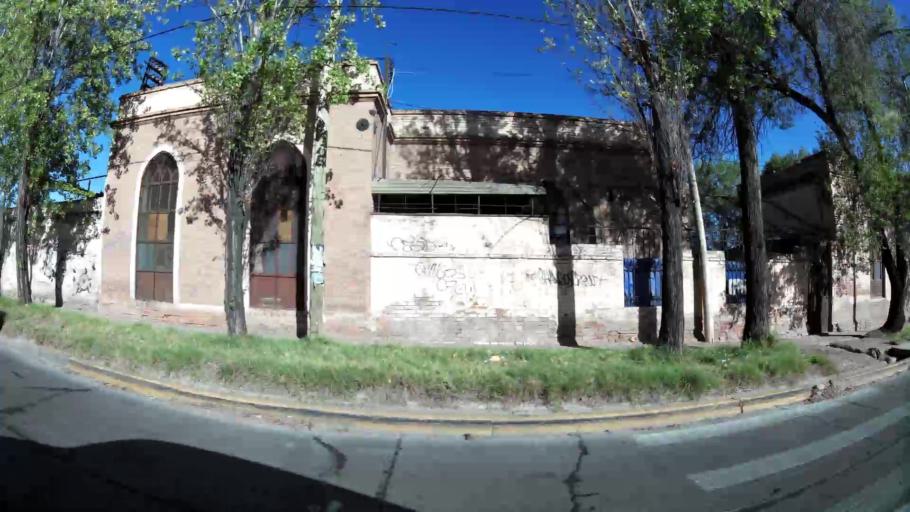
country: AR
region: Mendoza
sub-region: Departamento de Godoy Cruz
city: Godoy Cruz
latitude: -32.9327
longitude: -68.8397
